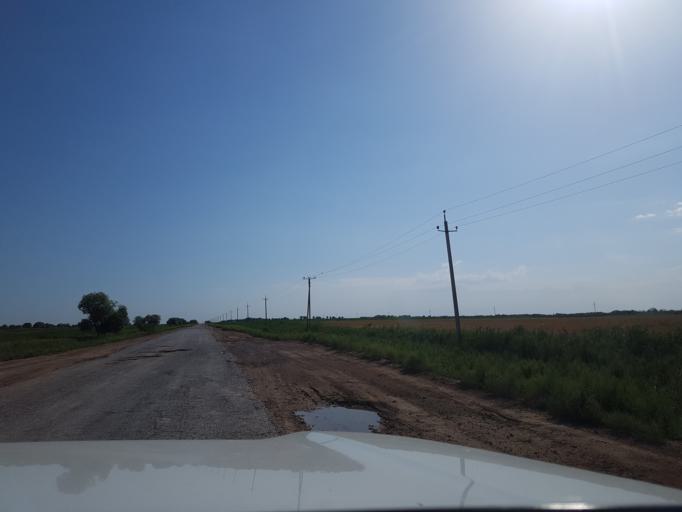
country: TM
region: Dasoguz
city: Koeneuergench
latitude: 42.0369
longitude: 58.8105
